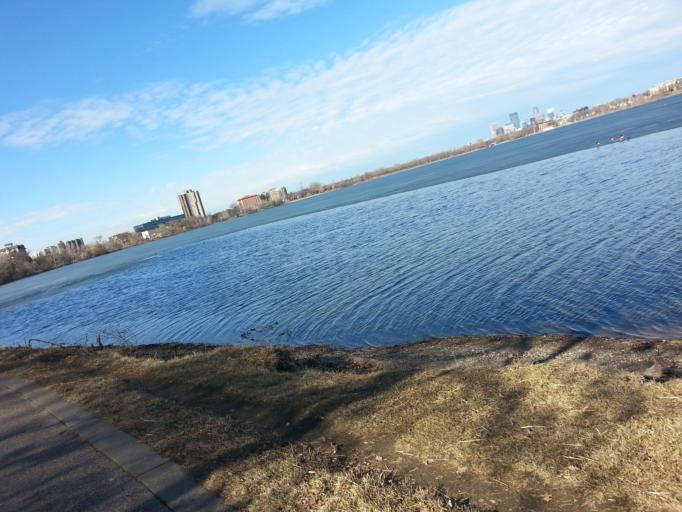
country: US
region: Minnesota
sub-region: Hennepin County
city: Saint Louis Park
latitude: 44.9389
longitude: -93.3193
